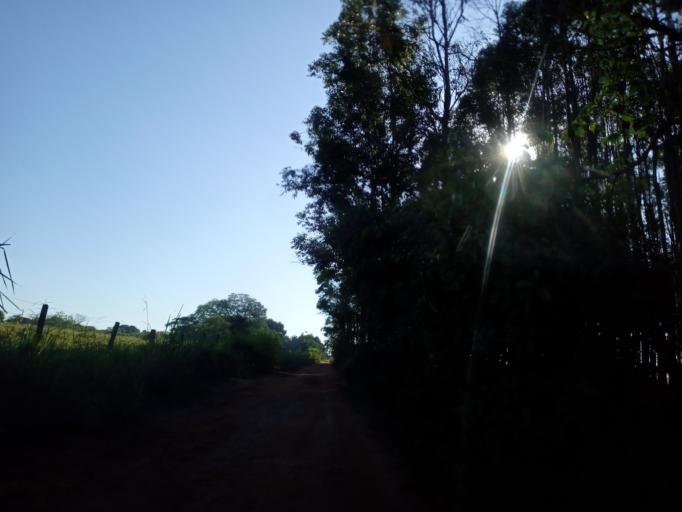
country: BR
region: Minas Gerais
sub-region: Ituiutaba
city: Ituiutaba
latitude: -18.9783
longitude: -49.5049
